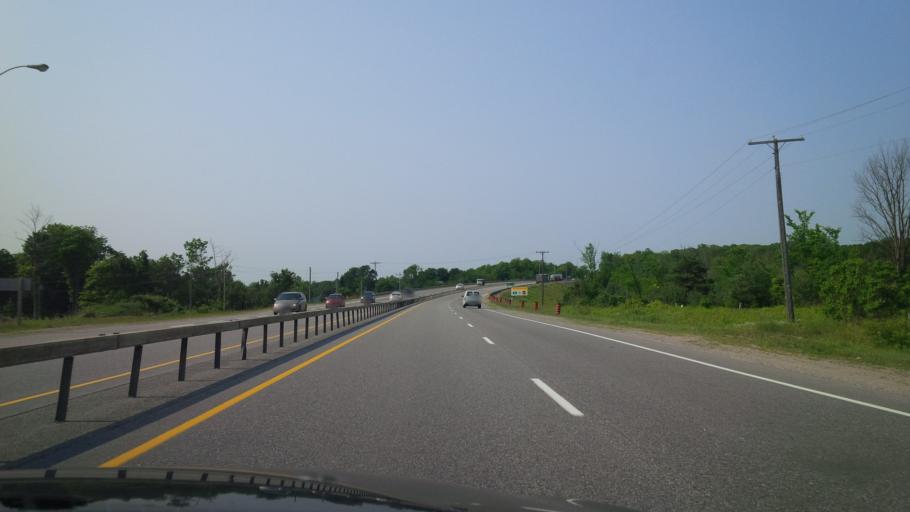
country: CA
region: Ontario
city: Orillia
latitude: 44.6490
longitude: -79.4184
